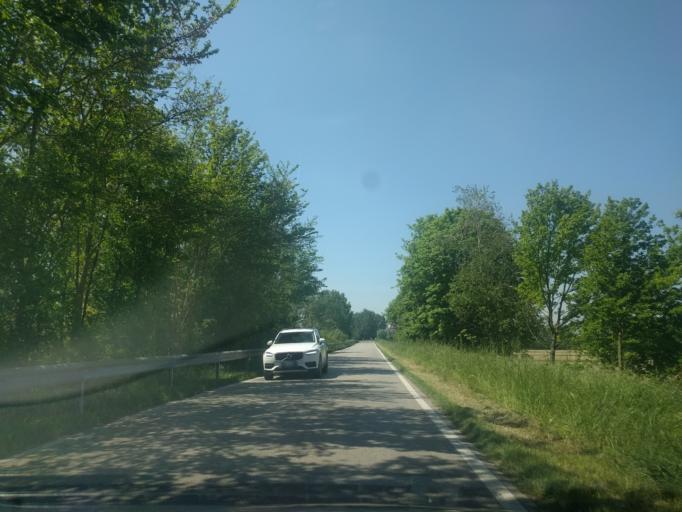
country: IT
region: Veneto
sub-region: Provincia di Rovigo
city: Villanova Marchesana
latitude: 45.0382
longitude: 11.9606
